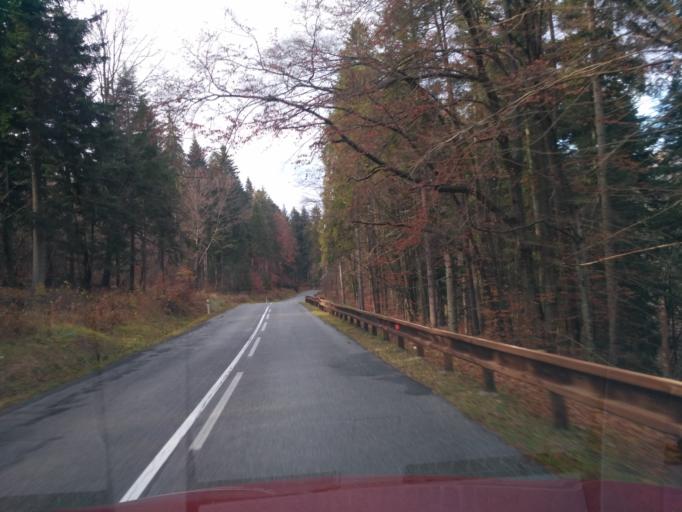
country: SK
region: Kosicky
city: Medzev
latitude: 48.7928
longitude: 20.7509
